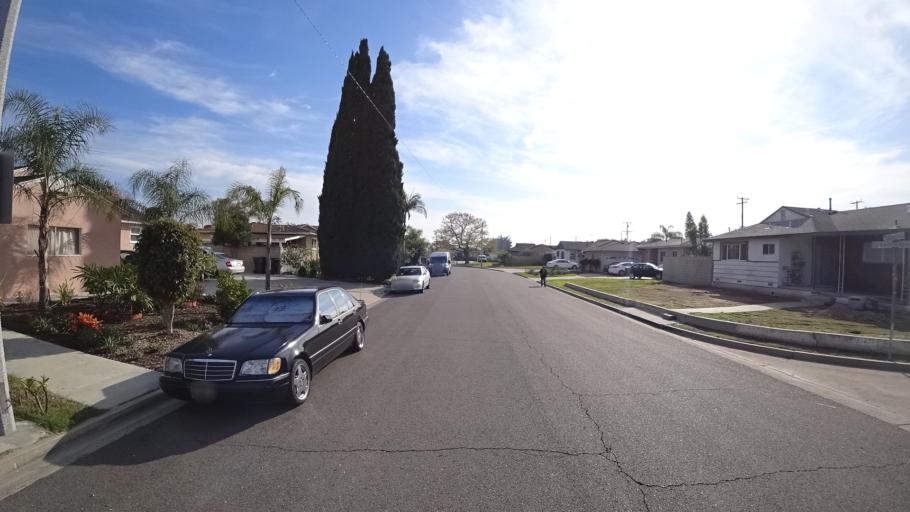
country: US
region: California
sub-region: Orange County
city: Garden Grove
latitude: 33.7704
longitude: -117.9047
